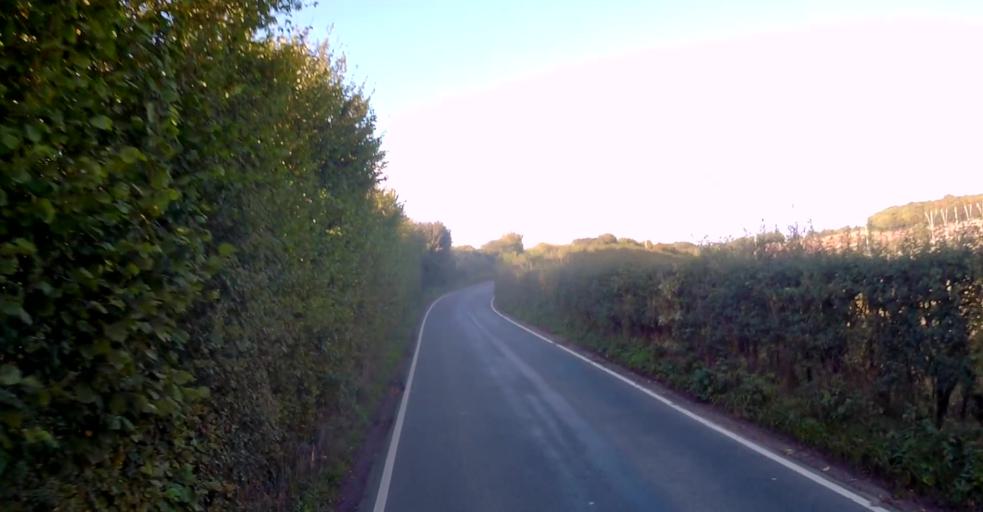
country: GB
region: England
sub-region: Hampshire
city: Long Sutton
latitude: 51.2326
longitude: -0.9270
